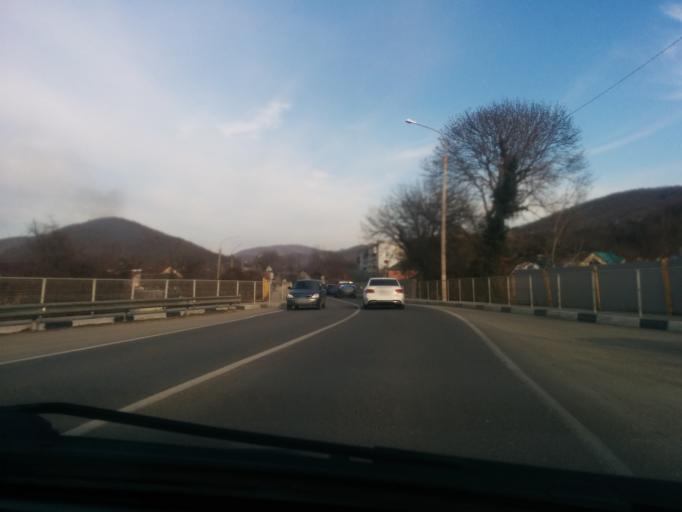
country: RU
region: Krasnodarskiy
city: Novomikhaylovskiy
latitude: 44.2563
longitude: 38.8533
